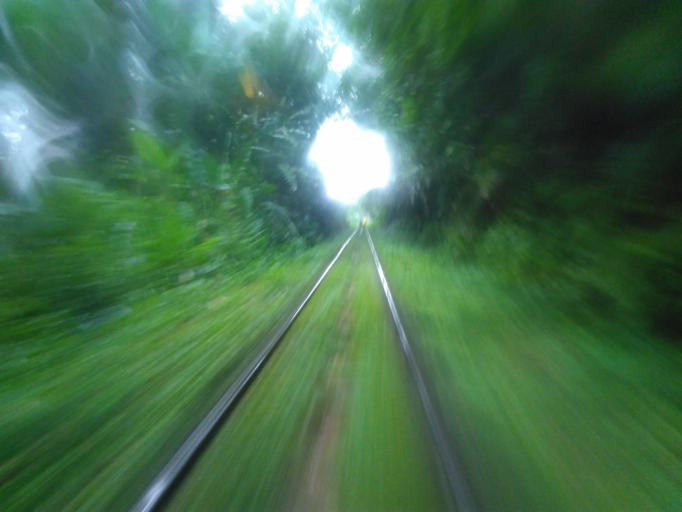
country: CO
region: Valle del Cauca
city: Buenaventura
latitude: 3.8480
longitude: -76.8623
